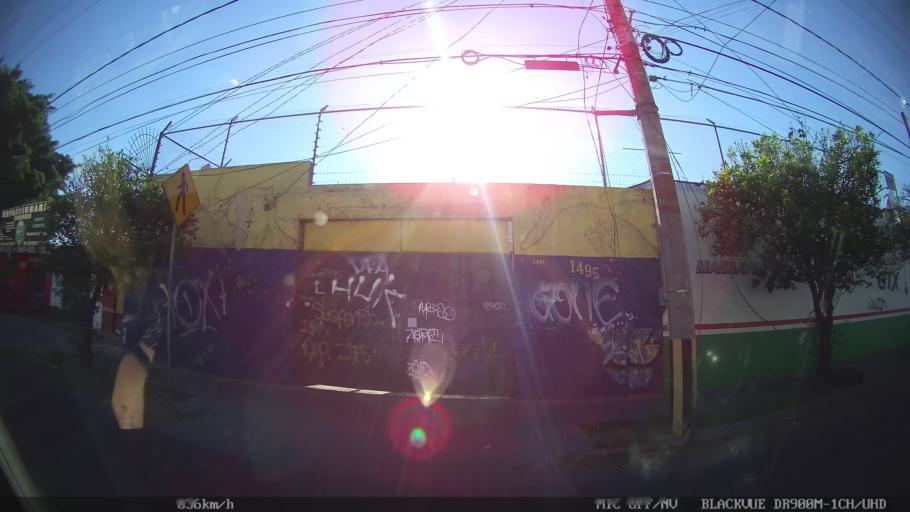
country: MX
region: Jalisco
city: Tlaquepaque
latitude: 20.6934
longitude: -103.3235
